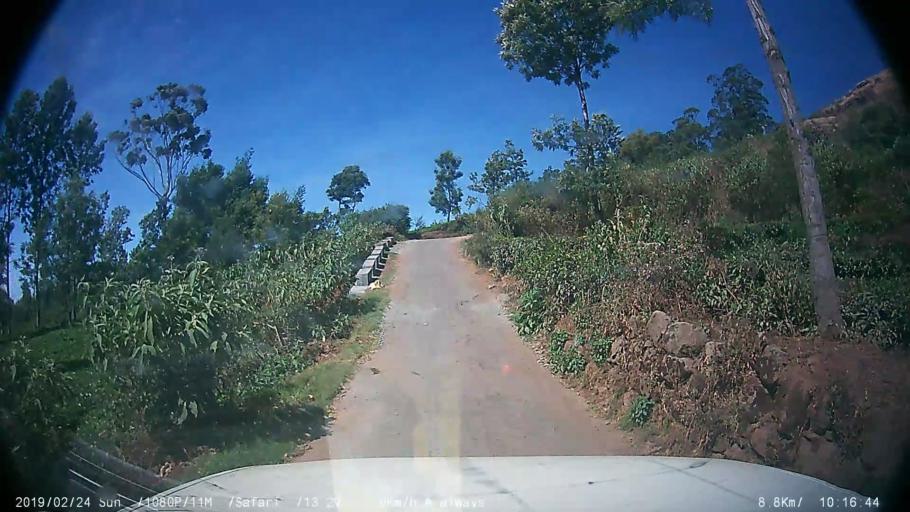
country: IN
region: Tamil Nadu
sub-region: Nilgiri
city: Ooty
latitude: 11.3862
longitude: 76.7235
